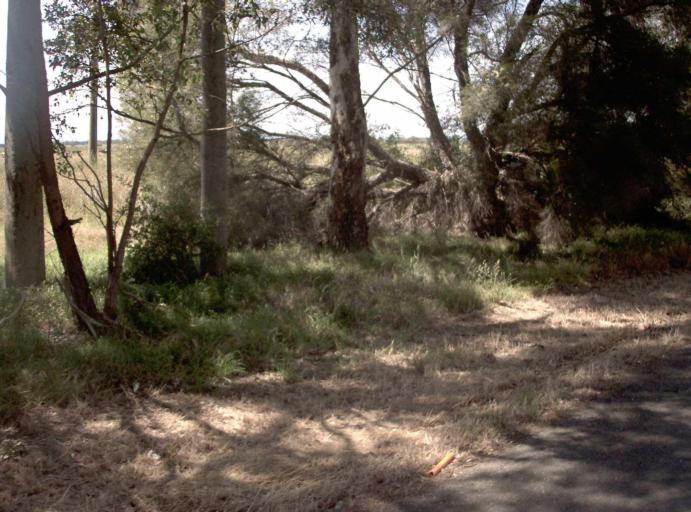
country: AU
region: Victoria
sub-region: Wellington
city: Heyfield
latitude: -38.1107
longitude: 146.8873
